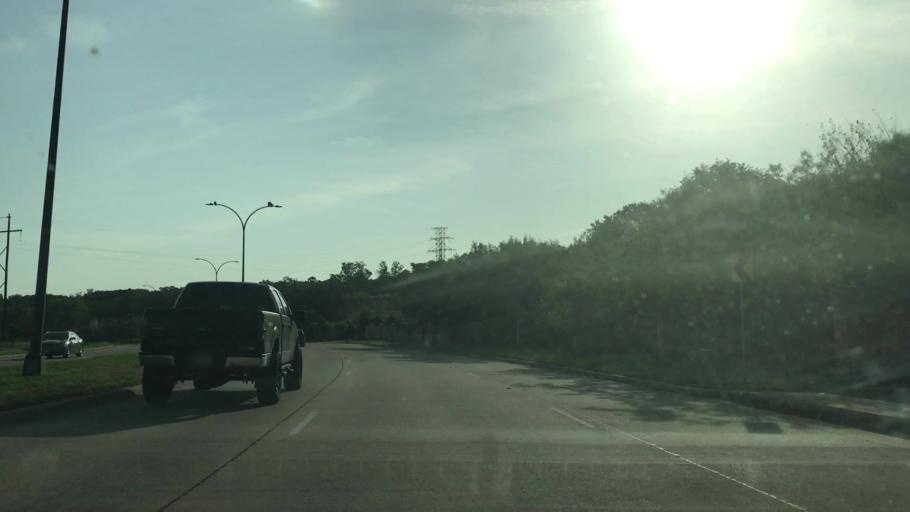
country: US
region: Texas
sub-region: Tarrant County
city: Arlington
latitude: 32.7714
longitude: -97.1388
